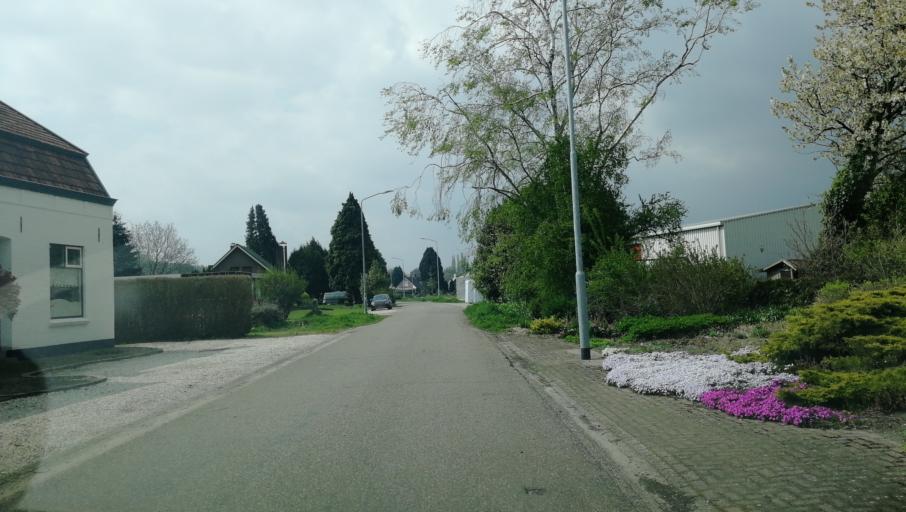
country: NL
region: Limburg
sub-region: Gemeente Venlo
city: Venlo
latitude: 51.3835
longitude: 6.2065
